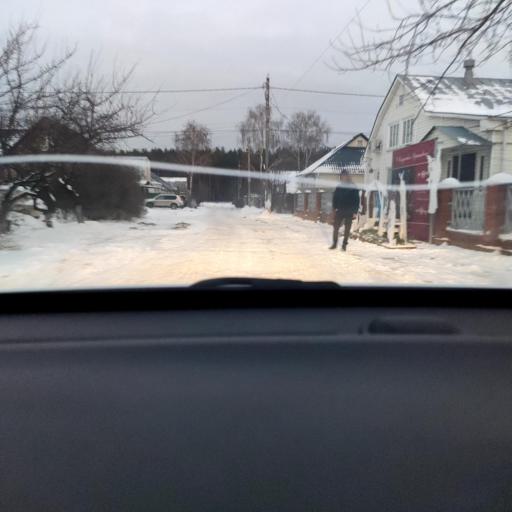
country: RU
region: Voronezj
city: Somovo
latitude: 51.7402
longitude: 39.2794
